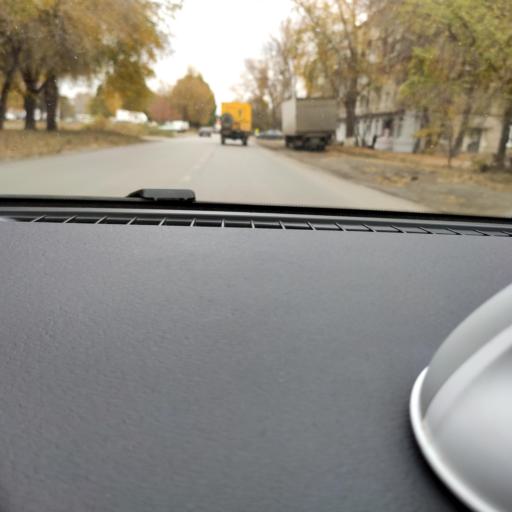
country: RU
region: Samara
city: Petra-Dubrava
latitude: 53.2479
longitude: 50.3098
